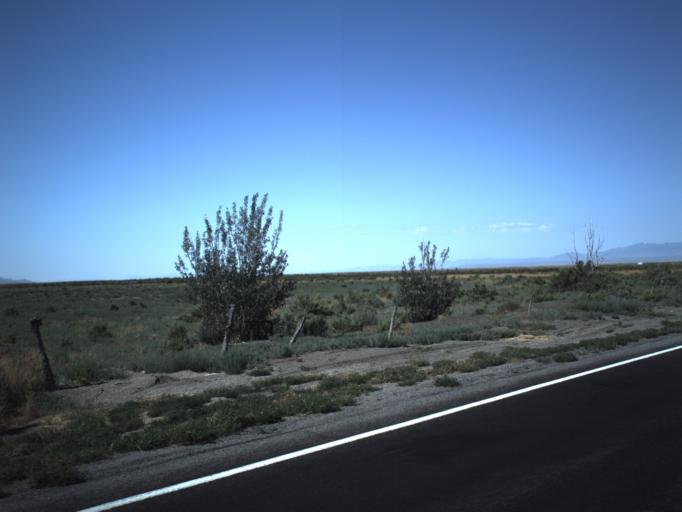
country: US
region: Utah
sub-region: Millard County
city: Delta
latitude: 39.3309
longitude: -112.7052
